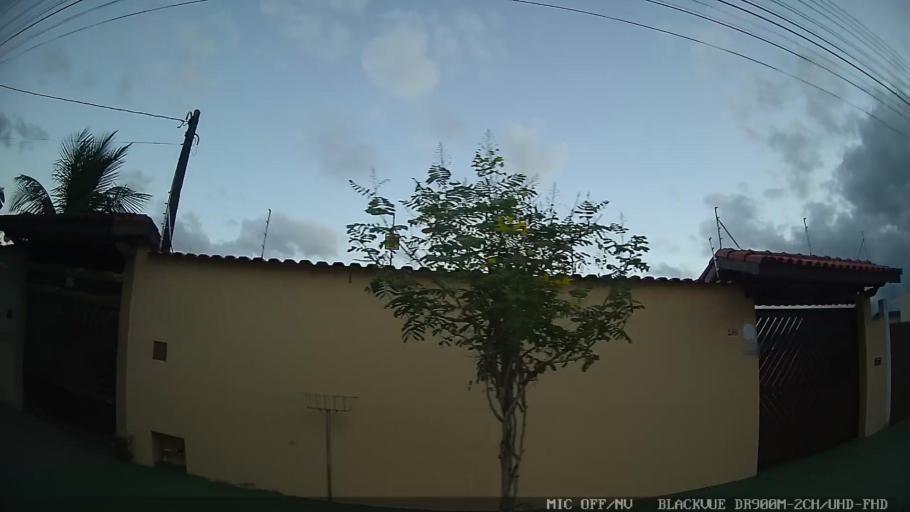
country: BR
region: Sao Paulo
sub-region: Caraguatatuba
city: Caraguatatuba
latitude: -23.6633
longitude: -45.4405
